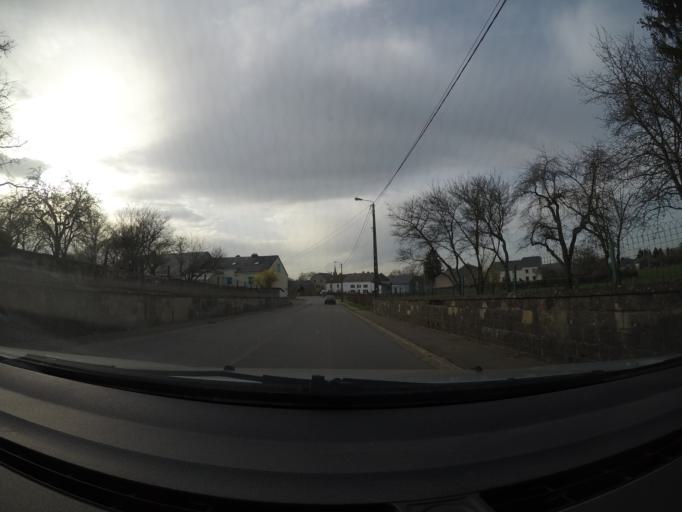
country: BE
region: Wallonia
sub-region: Province du Luxembourg
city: Messancy
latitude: 49.6311
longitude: 5.8360
